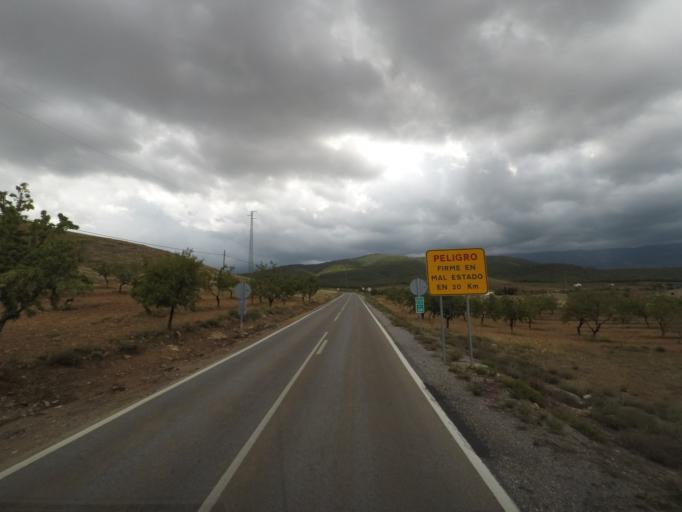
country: ES
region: Andalusia
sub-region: Provincia de Granada
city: Ferreira
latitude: 37.1811
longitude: -3.0585
